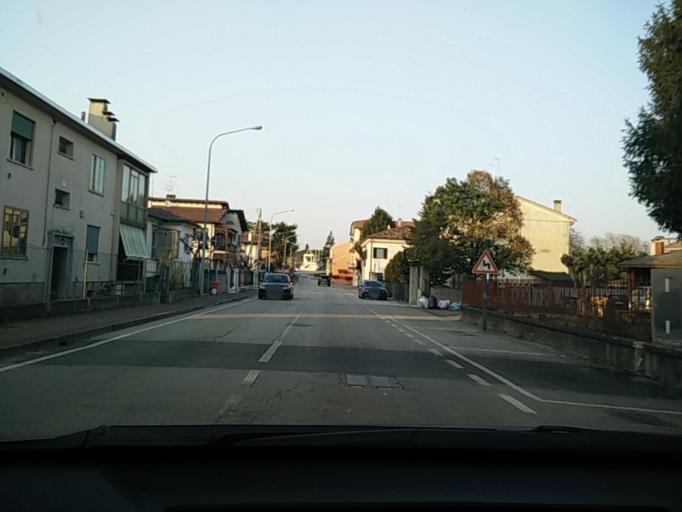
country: IT
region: Veneto
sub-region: Provincia di Venezia
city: Fossalta di Piave
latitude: 45.6480
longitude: 12.5139
